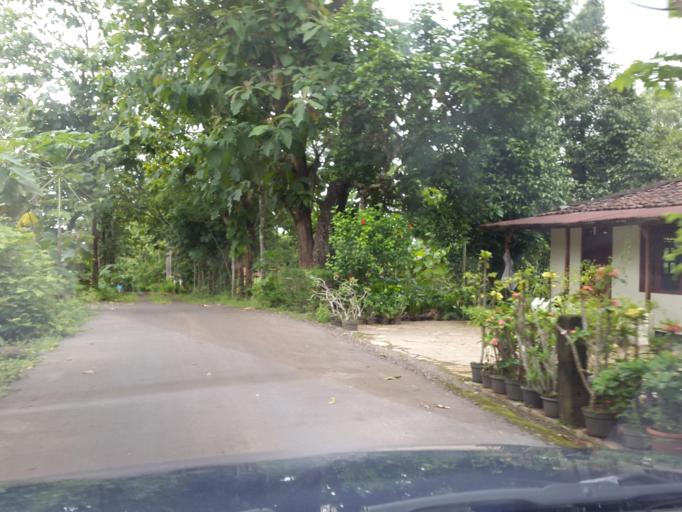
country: ID
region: Daerah Istimewa Yogyakarta
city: Wonosari
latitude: -7.9257
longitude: 110.6821
